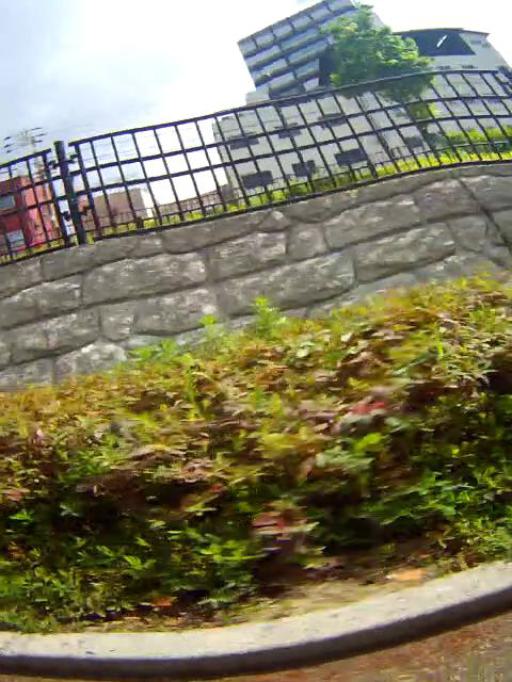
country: JP
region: Osaka
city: Osaka-shi
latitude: 34.7020
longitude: 135.5220
